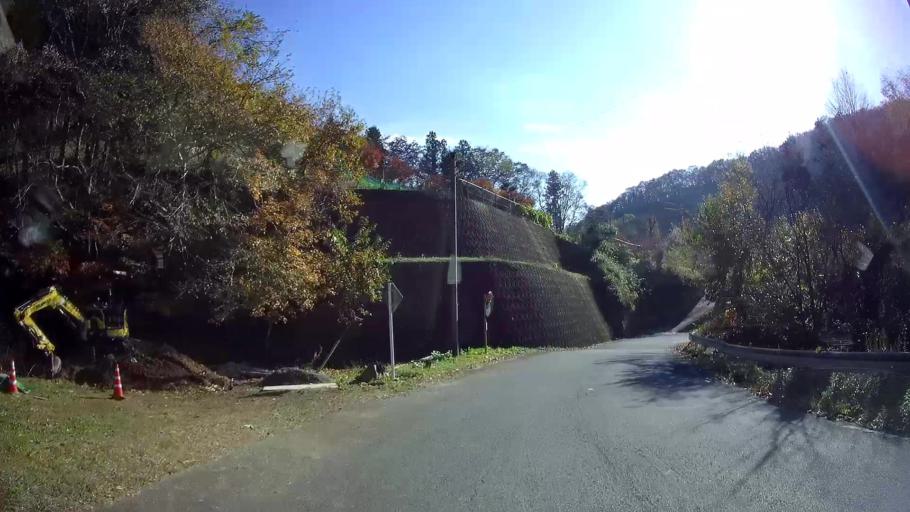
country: JP
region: Yamanashi
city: Uenohara
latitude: 35.5943
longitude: 139.1252
